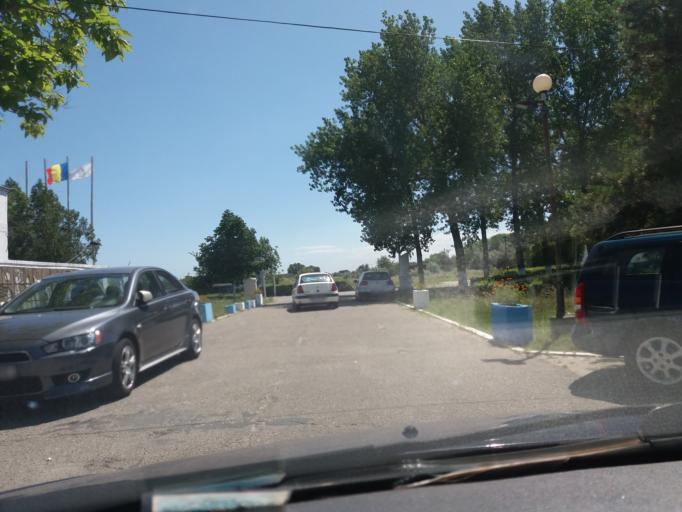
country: RO
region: Constanta
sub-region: Comuna Navodari
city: Navodari
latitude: 44.3196
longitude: 28.6290
